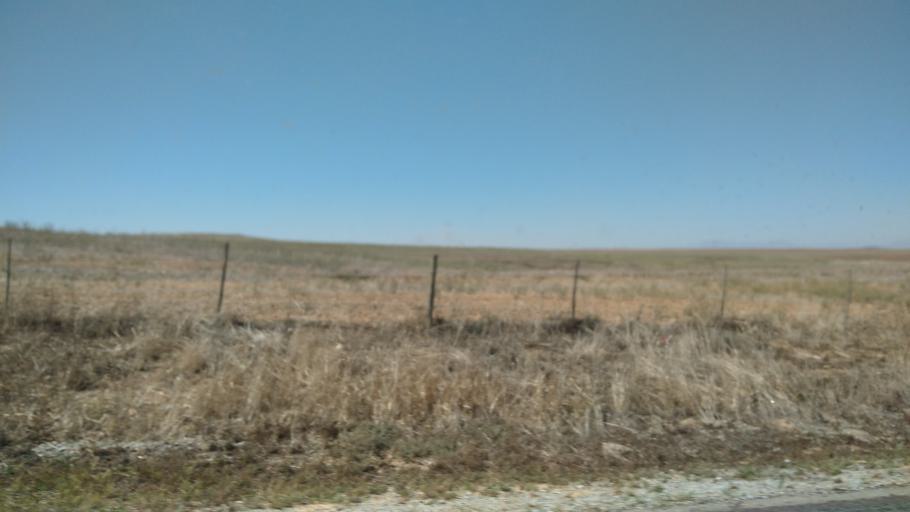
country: ZA
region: Western Cape
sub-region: West Coast District Municipality
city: Moorreesburg
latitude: -33.1829
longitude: 18.4955
